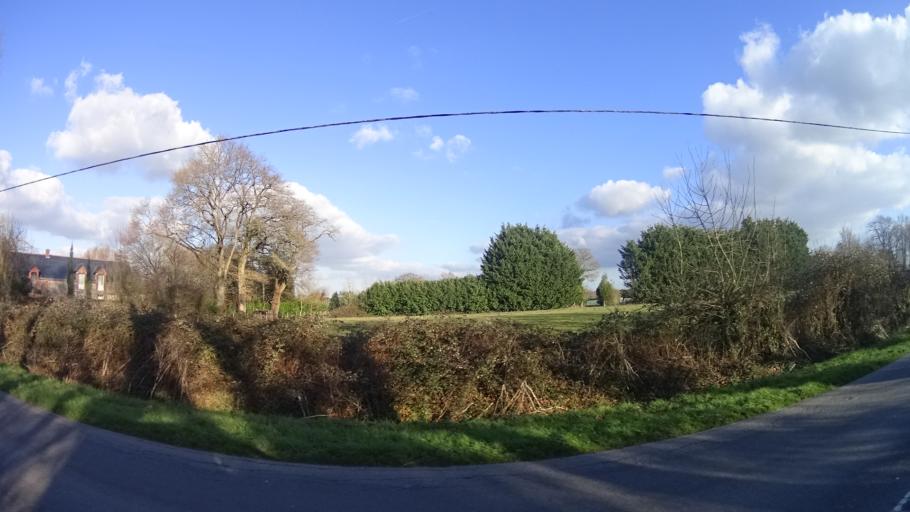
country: FR
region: Pays de la Loire
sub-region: Departement de la Loire-Atlantique
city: Plesse
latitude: 47.5337
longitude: -1.8873
